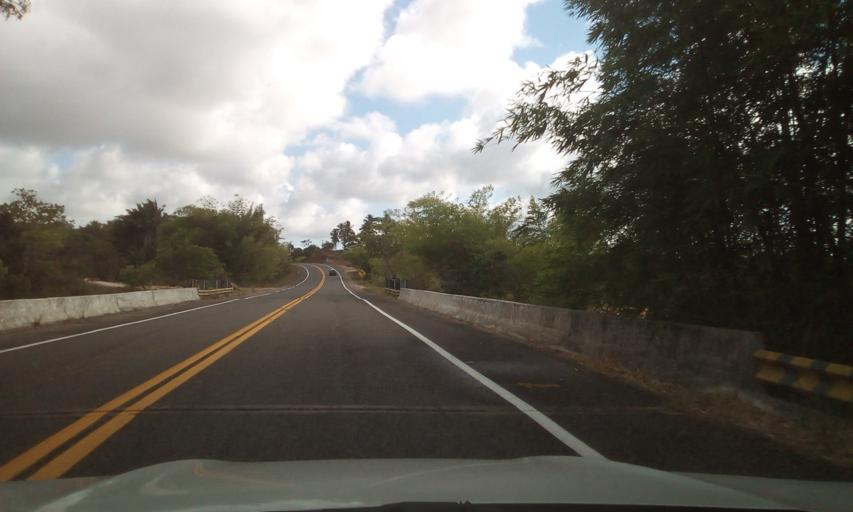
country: BR
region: Sergipe
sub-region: Indiaroba
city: Indiaroba
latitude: -11.6538
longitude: -37.5465
